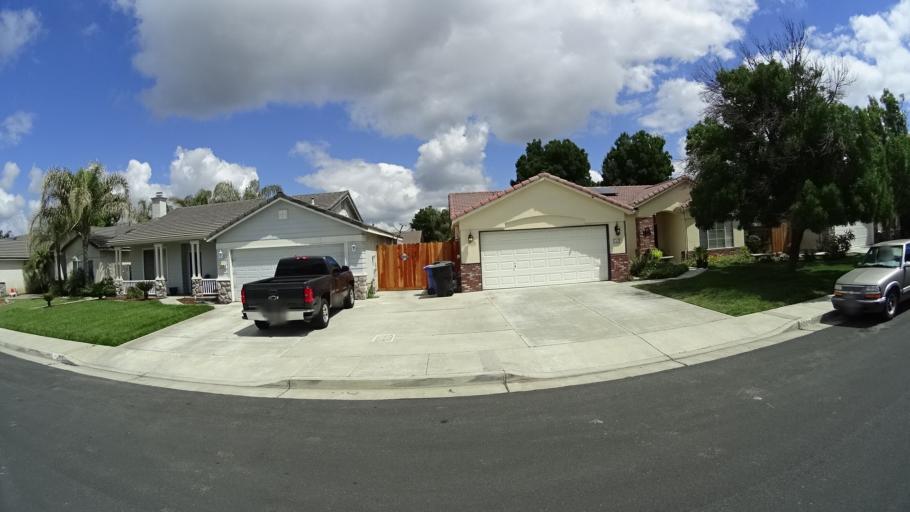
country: US
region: California
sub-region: Kings County
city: Lucerne
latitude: 36.3600
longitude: -119.6604
